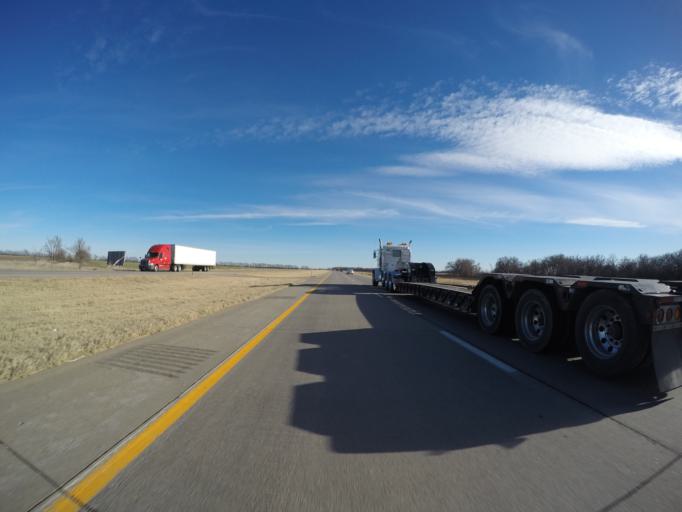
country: US
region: Kansas
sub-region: McPherson County
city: Moundridge
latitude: 38.2608
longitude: -97.5551
